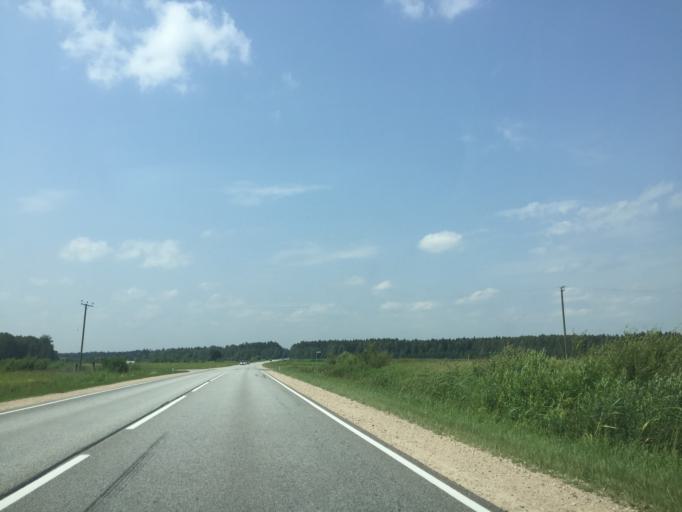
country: LV
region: Kekava
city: Kekava
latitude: 56.8095
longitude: 24.1802
